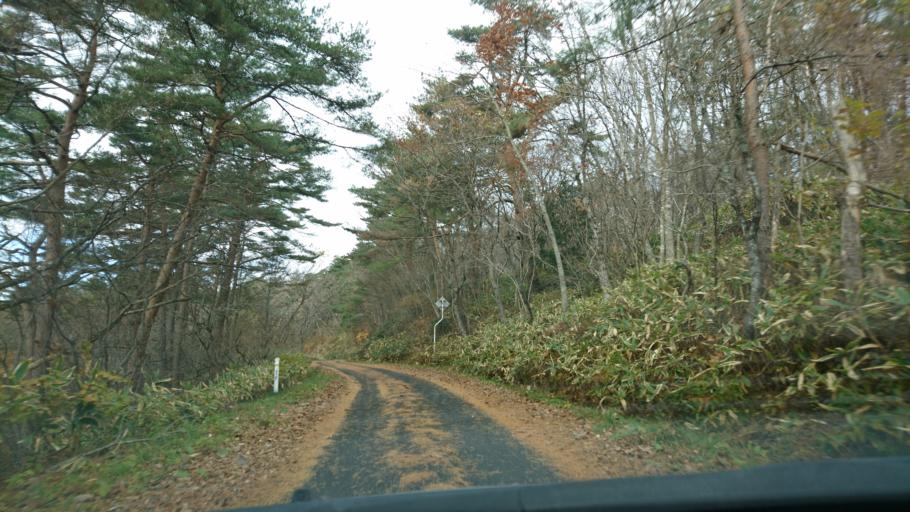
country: JP
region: Iwate
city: Ichinoseki
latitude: 39.0019
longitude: 141.1909
